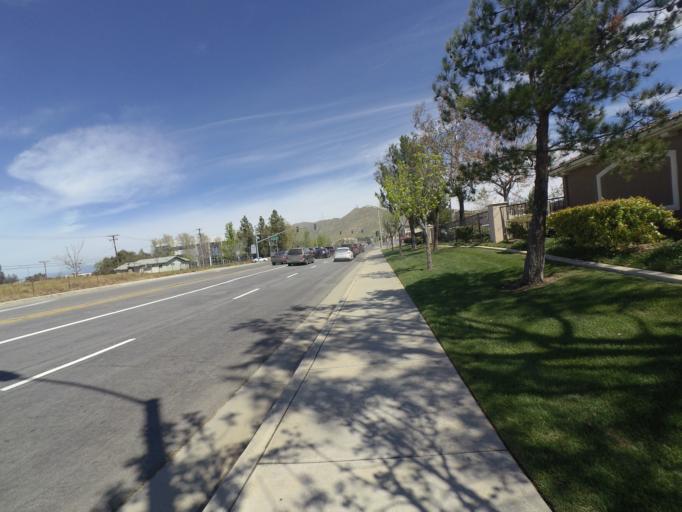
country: US
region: California
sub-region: Riverside County
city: March Air Force Base
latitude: 33.9306
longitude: -117.2787
